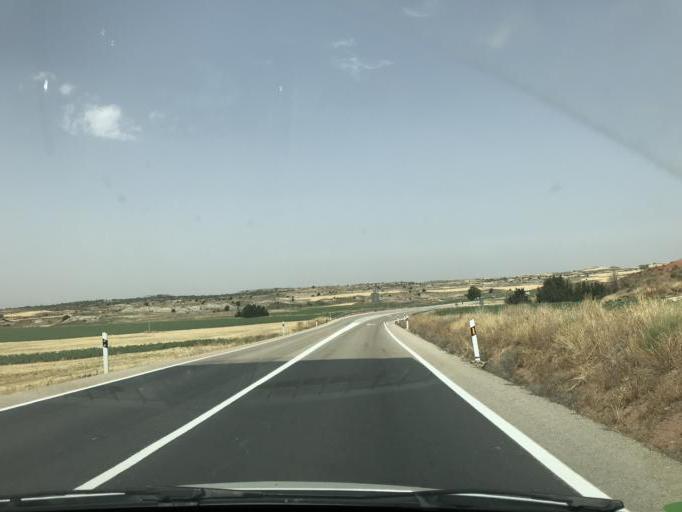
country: ES
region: Castille-La Mancha
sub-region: Provincia de Cuenca
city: Villar de Domingo Garcia
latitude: 40.2439
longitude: -2.3008
